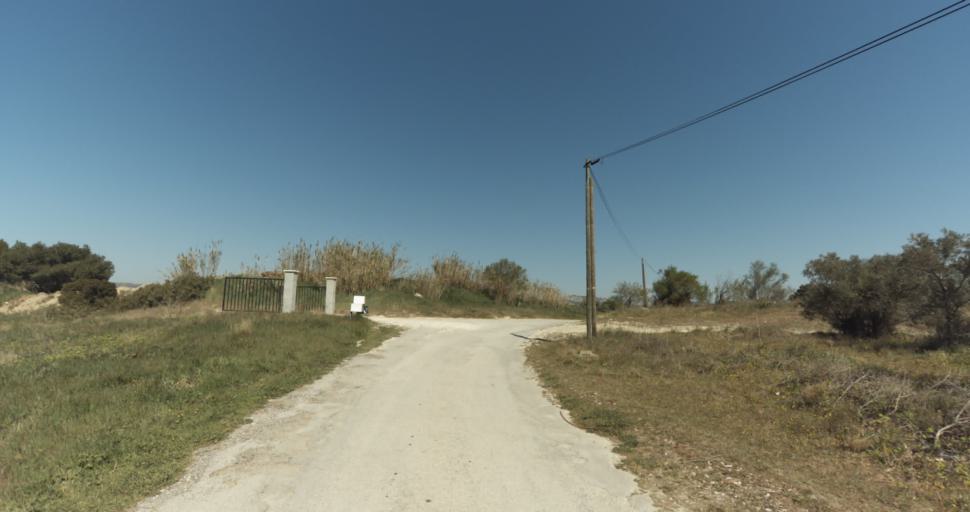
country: FR
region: Provence-Alpes-Cote d'Azur
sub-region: Departement des Bouches-du-Rhone
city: Pelissanne
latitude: 43.6182
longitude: 5.1567
